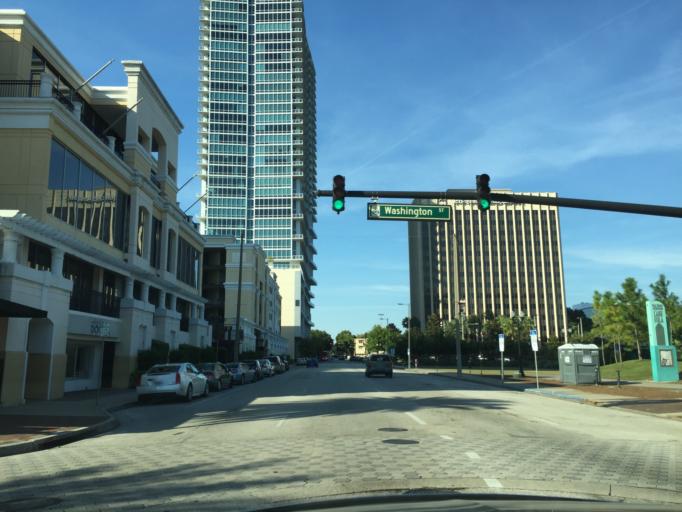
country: US
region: Florida
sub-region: Orange County
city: Orlando
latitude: 28.5435
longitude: -81.3759
